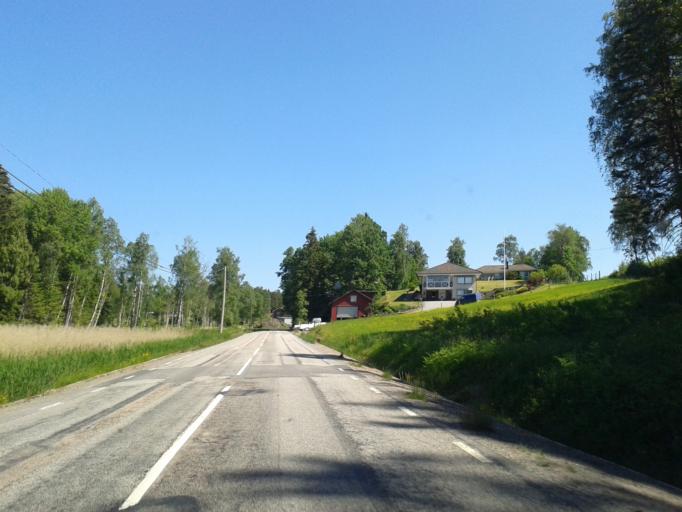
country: SE
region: Vaestra Goetaland
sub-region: Orust
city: Henan
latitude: 58.2349
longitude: 11.6958
